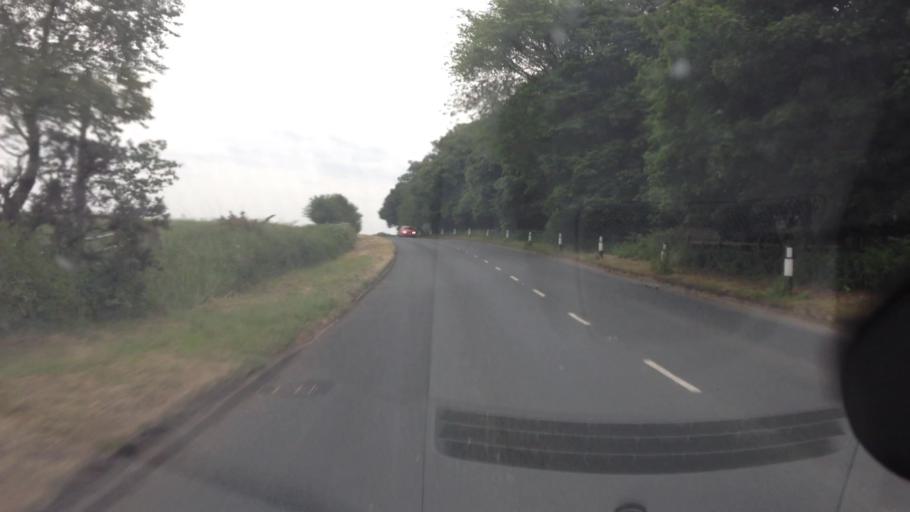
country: GB
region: England
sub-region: City and Borough of Wakefield
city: Woolley
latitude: 53.6116
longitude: -1.5340
